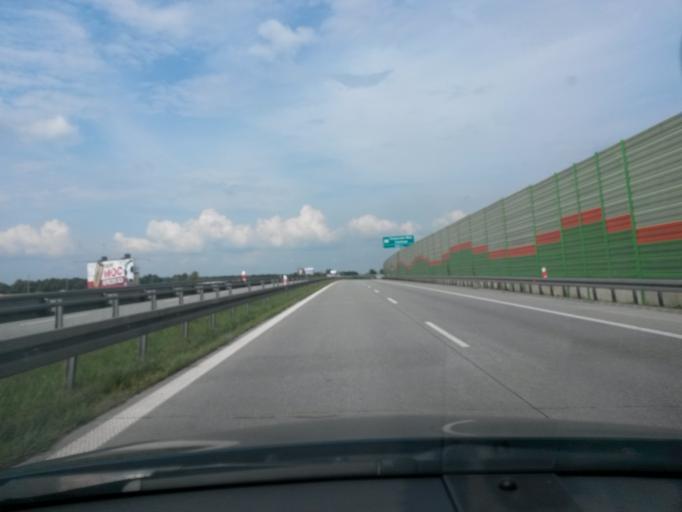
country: PL
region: Lodz Voivodeship
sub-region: Powiat tomaszowski
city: Tomaszow Mazowiecki
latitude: 51.5405
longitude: 19.9647
